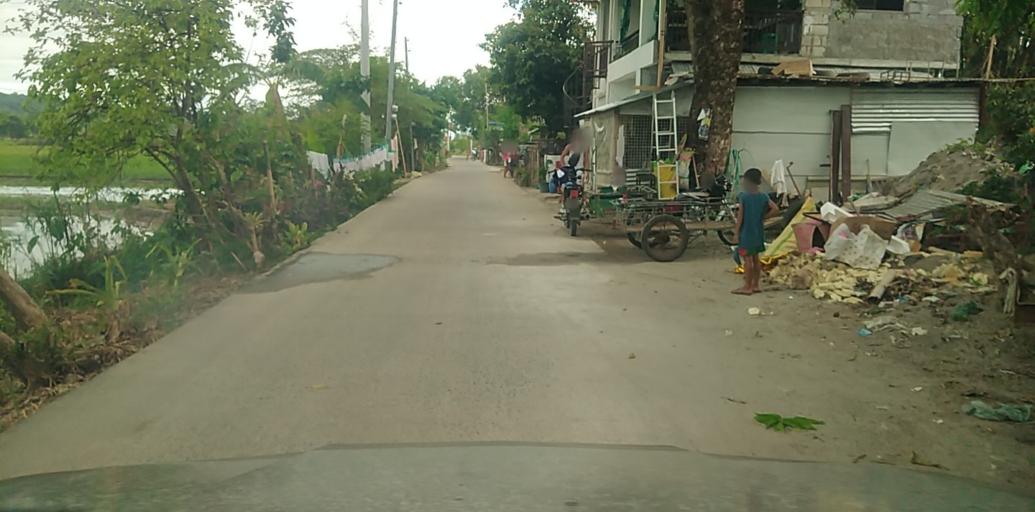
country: PH
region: Central Luzon
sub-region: Province of Pampanga
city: Panlinlang
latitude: 15.1805
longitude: 120.6997
